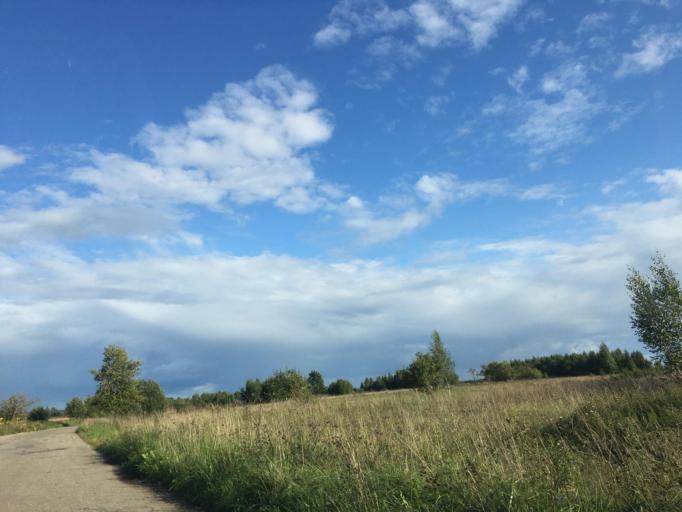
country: RU
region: Pskov
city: Izborsk
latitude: 57.7698
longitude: 27.9831
